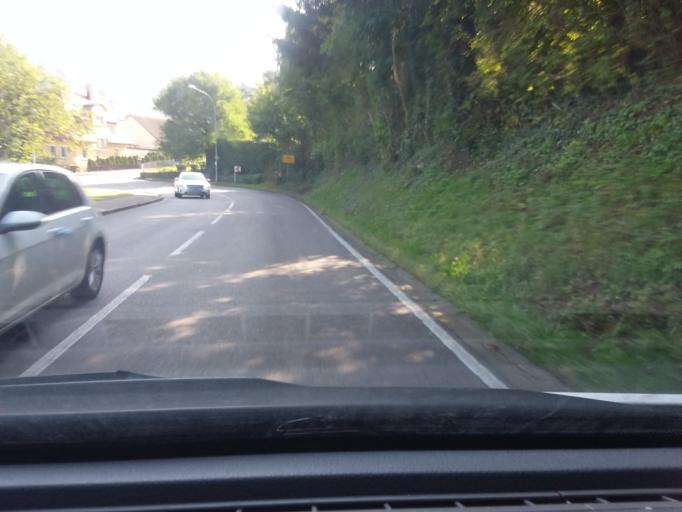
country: DE
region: Baden-Wuerttemberg
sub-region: Regierungsbezirk Stuttgart
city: Geislingen an der Steige
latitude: 48.6151
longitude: 9.8344
